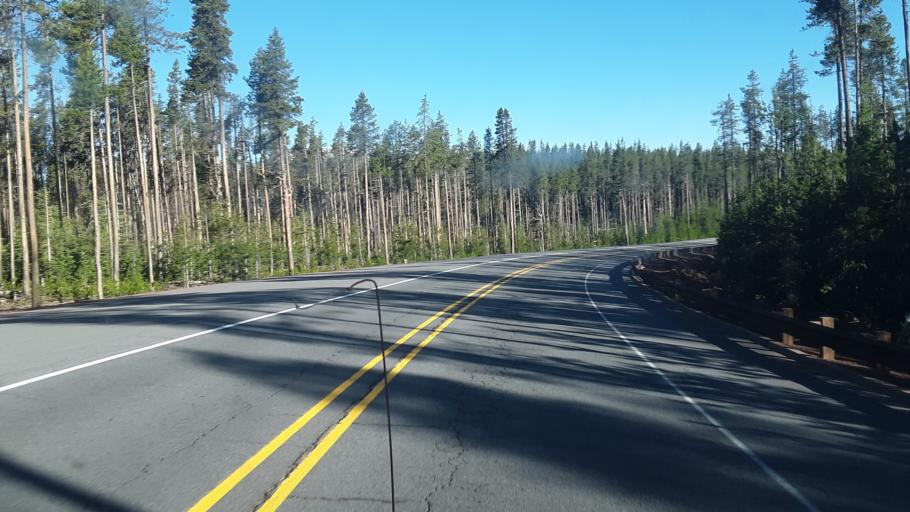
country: US
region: Oregon
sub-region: Lane County
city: Oakridge
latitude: 43.1003
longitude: -122.1295
